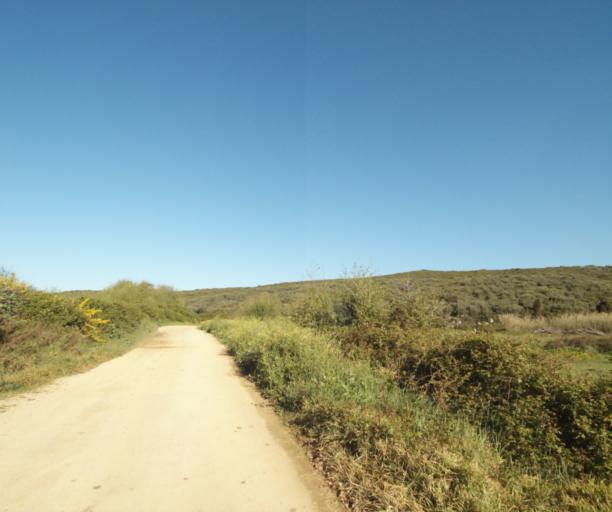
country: FR
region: Corsica
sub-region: Departement de la Corse-du-Sud
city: Propriano
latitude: 41.6637
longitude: 8.8936
